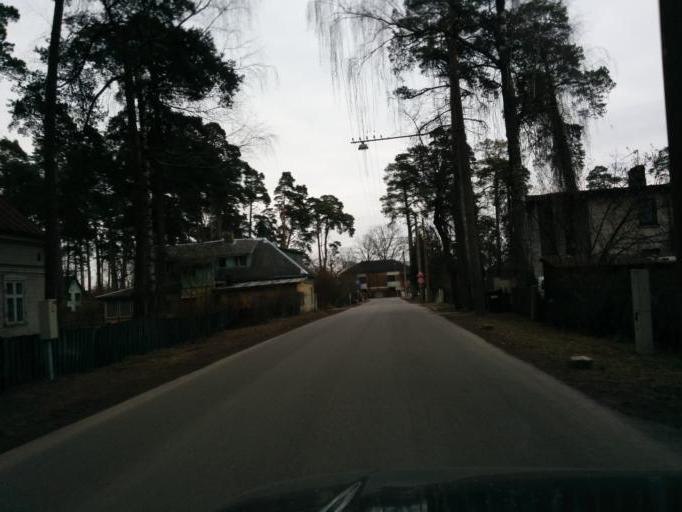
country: LV
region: Babite
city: Pinki
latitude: 56.9939
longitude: 23.9129
